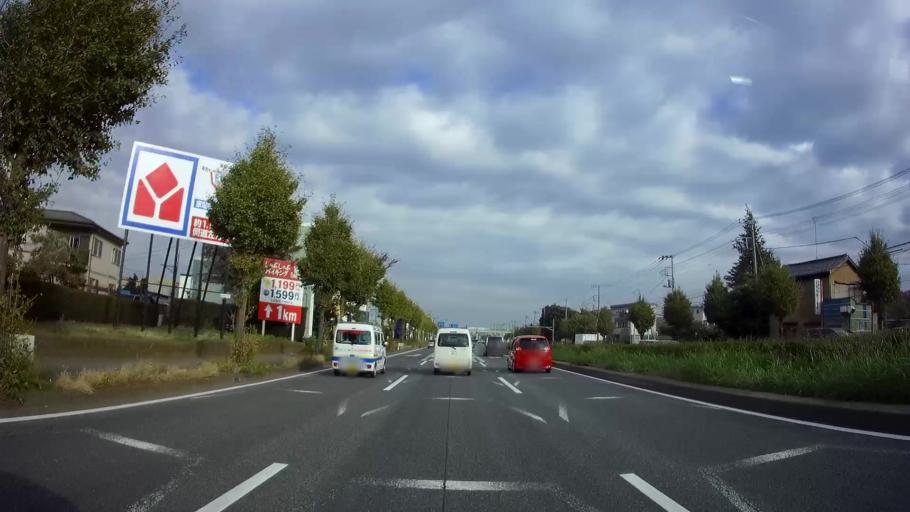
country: JP
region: Saitama
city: Yono
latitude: 35.9124
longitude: 139.5934
